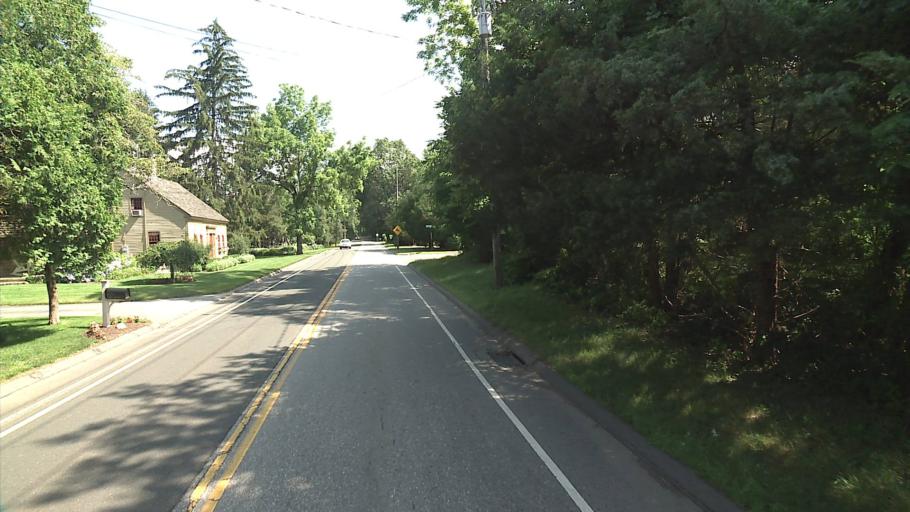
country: US
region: Connecticut
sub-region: Middlesex County
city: Westbrook Center
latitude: 41.3233
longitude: -72.4296
